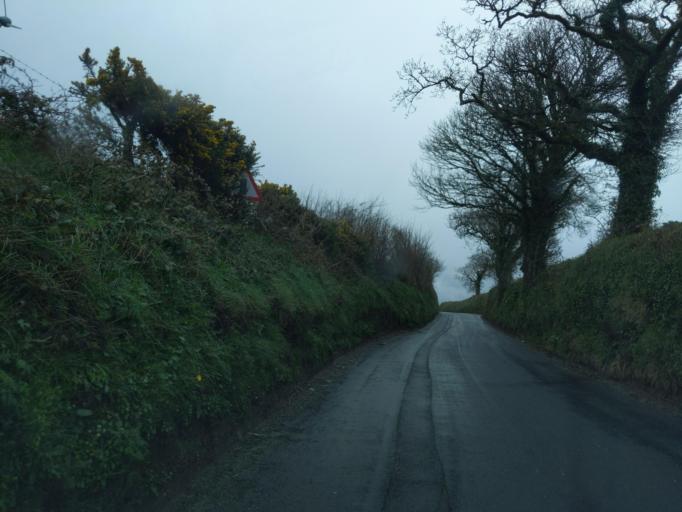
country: GB
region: England
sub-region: Cornwall
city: North Hill
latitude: 50.5834
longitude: -4.4333
